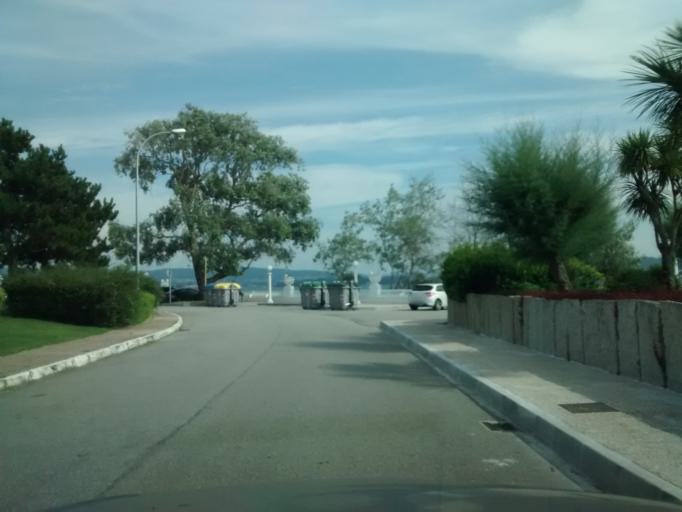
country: ES
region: Galicia
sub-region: Provincia de Pontevedra
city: O Grove
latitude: 42.4826
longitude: -8.8482
